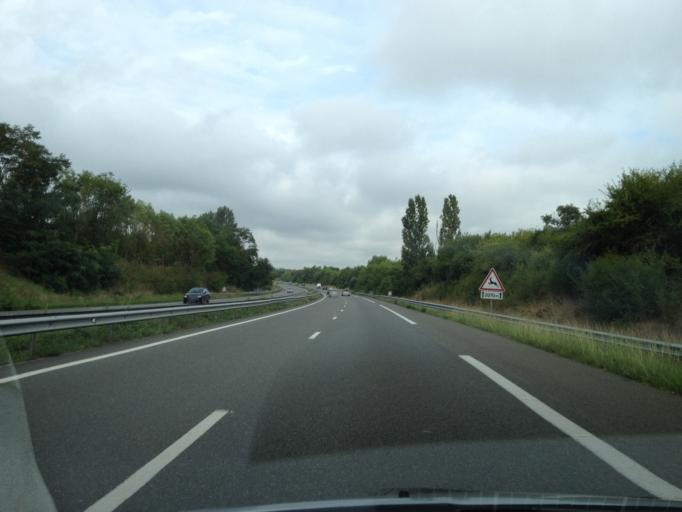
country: FR
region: Midi-Pyrenees
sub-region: Departement du Tarn-et-Garonne
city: Auvillar
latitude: 44.0575
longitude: 0.9471
